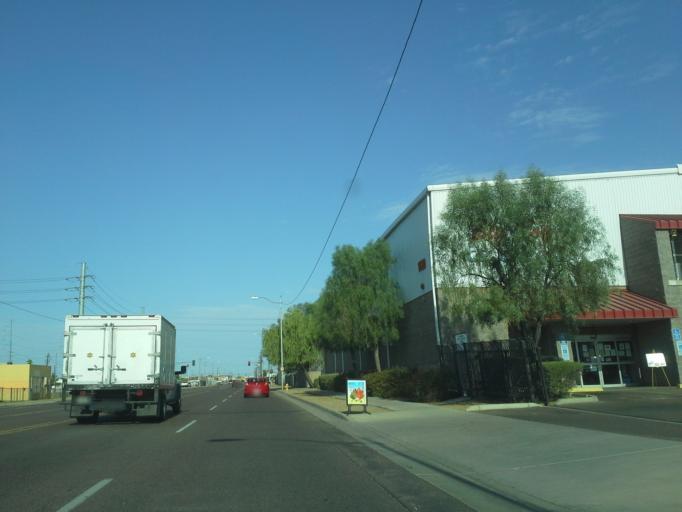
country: US
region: Arizona
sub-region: Maricopa County
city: Phoenix
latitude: 33.4415
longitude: -112.0937
